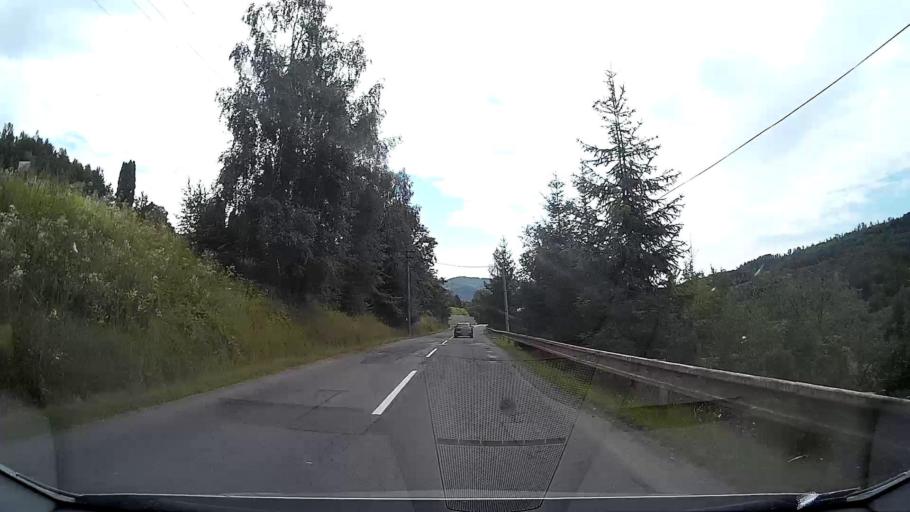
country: SK
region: Banskobystricky
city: Tisovec
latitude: 48.6243
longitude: 19.9532
